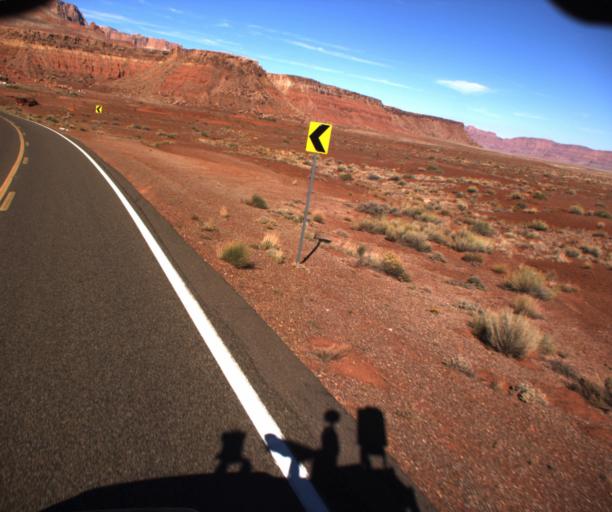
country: US
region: Arizona
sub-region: Coconino County
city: Page
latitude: 36.7353
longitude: -111.7555
